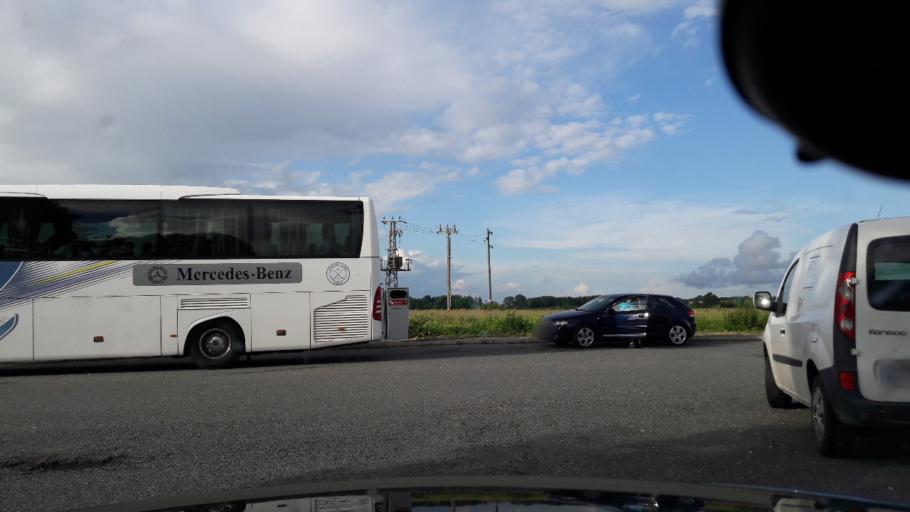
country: HR
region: Sisacko-Moslavacka
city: Lipovljani
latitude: 45.4016
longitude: 16.8614
